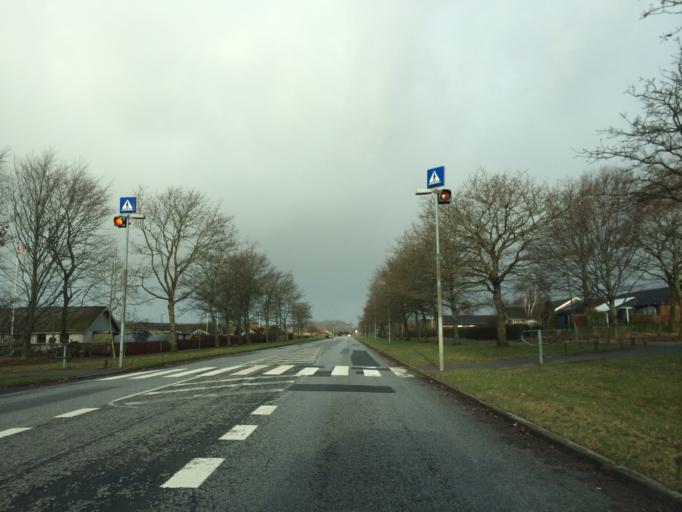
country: DK
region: Central Jutland
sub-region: Herning Kommune
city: Vildbjerg
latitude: 56.1901
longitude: 8.7635
